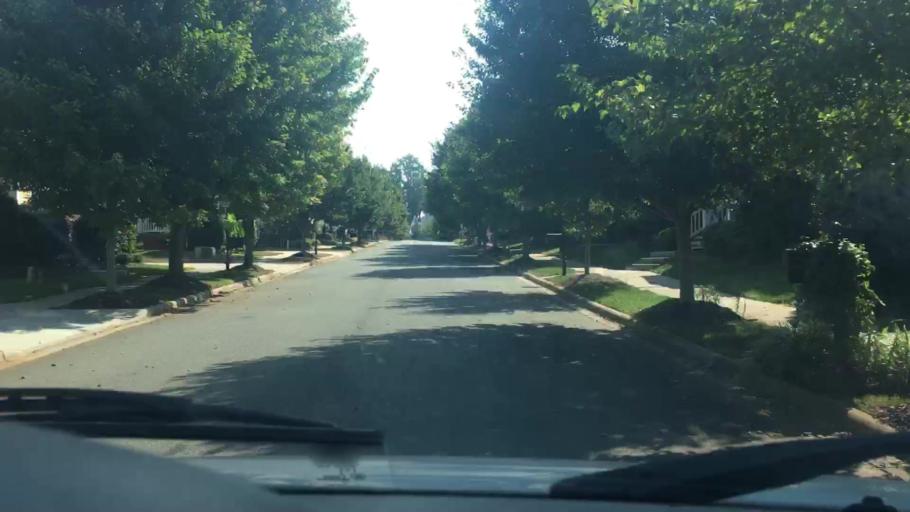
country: US
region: North Carolina
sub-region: Mecklenburg County
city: Huntersville
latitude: 35.4308
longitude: -80.8532
